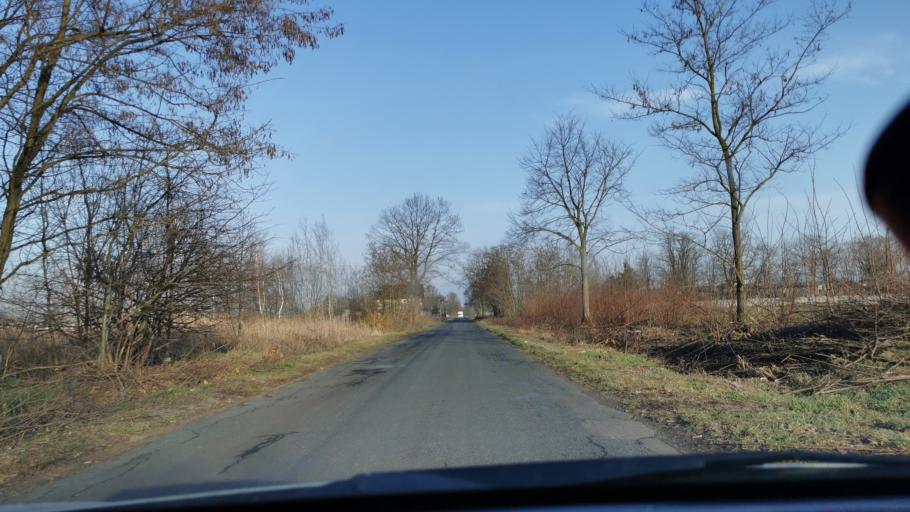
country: PL
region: Greater Poland Voivodeship
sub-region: Powiat kaliski
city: Opatowek
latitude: 51.6759
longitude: 18.2974
